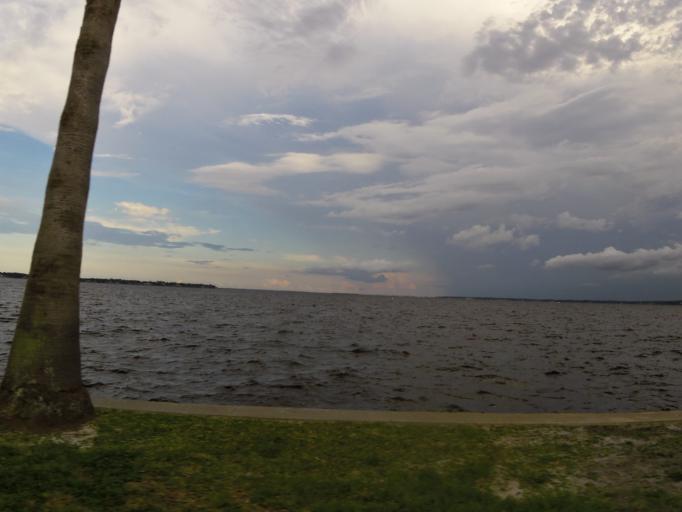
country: US
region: Florida
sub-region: Duval County
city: Jacksonville
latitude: 30.3092
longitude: -81.6828
